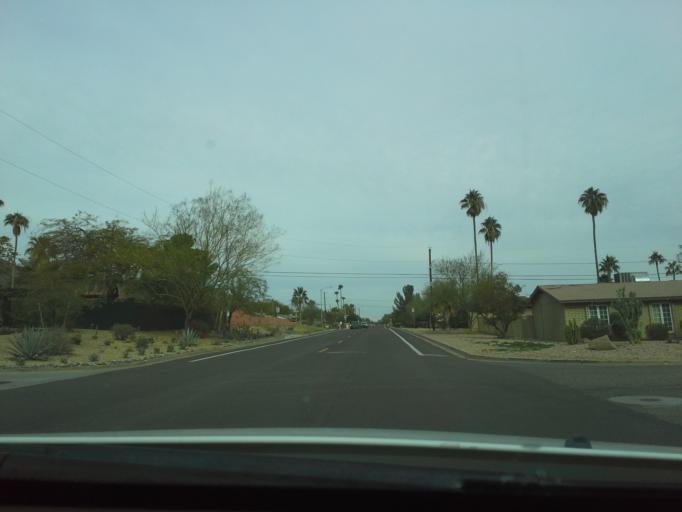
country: US
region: Arizona
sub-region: Maricopa County
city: Paradise Valley
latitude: 33.6075
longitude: -112.0219
